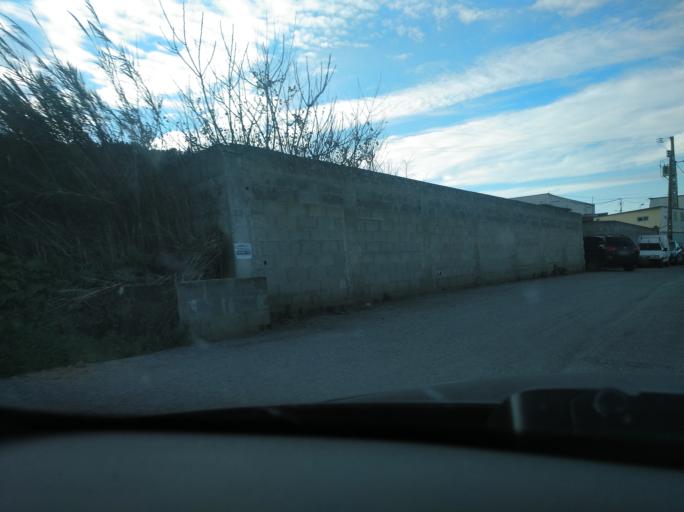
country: PT
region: Lisbon
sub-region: Loures
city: Unhos
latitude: 38.8342
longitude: -9.1220
